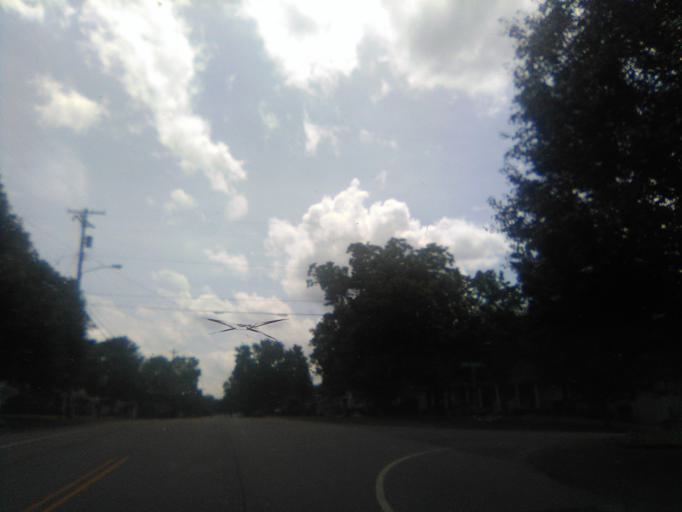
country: US
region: Tennessee
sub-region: Davidson County
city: Belle Meade
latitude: 36.0936
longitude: -86.8781
